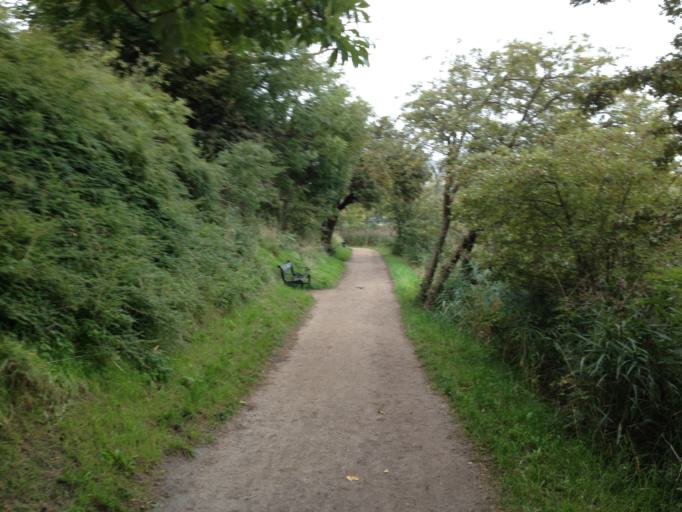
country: DK
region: Capital Region
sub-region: Kobenhavn
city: Christianshavn
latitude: 55.6699
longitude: 12.5843
